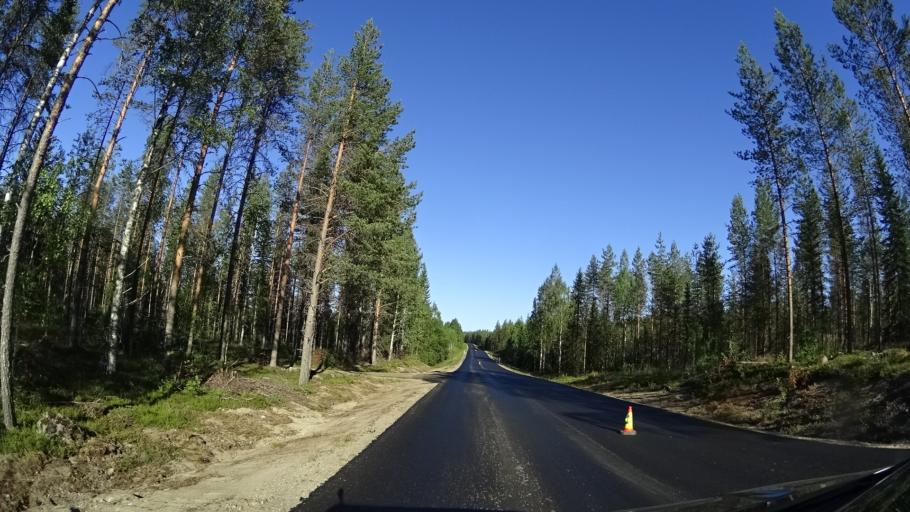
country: FI
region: North Karelia
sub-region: Pielisen Karjala
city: Valtimo
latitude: 63.5620
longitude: 28.5887
